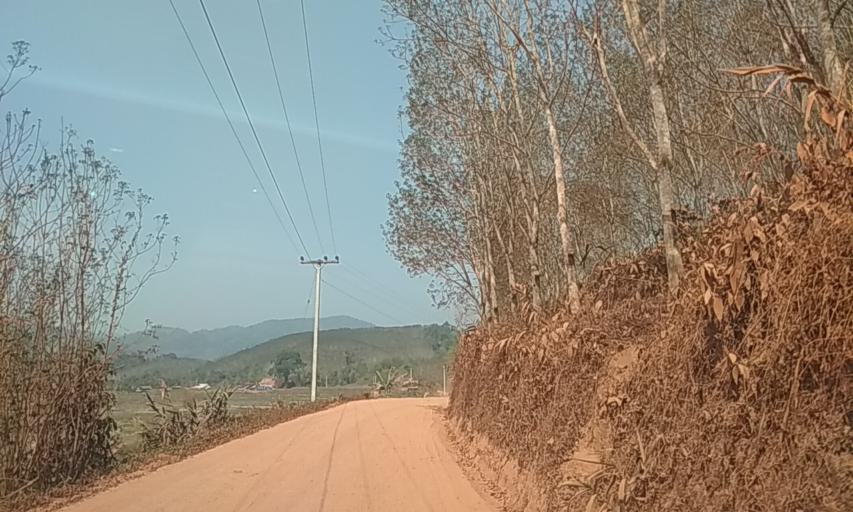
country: CN
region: Yunnan
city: Mengla
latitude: 21.5157
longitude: 101.8506
